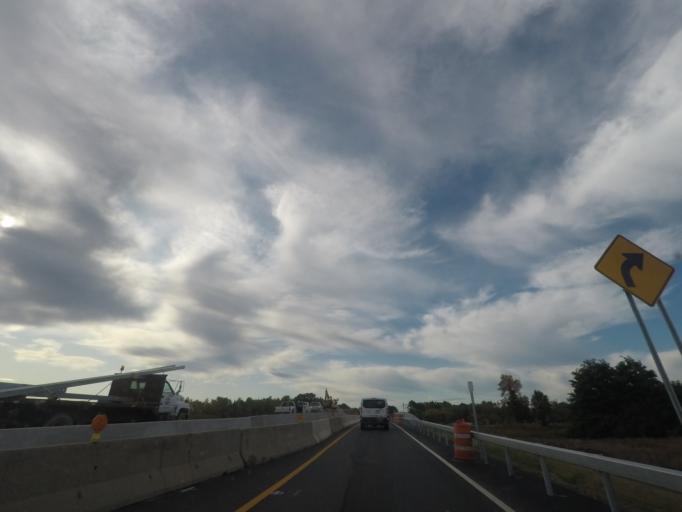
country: US
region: New York
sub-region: Albany County
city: Colonie
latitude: 42.7276
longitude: -73.8023
